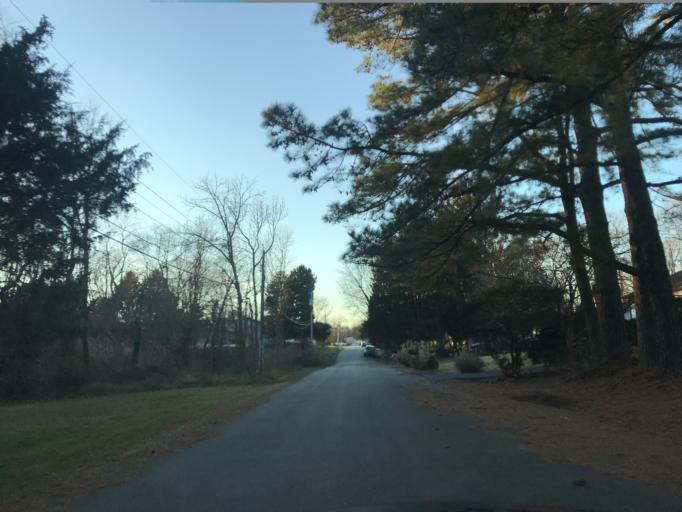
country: US
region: Maryland
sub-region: Baltimore County
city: Bowleys Quarters
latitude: 39.3710
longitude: -76.3456
